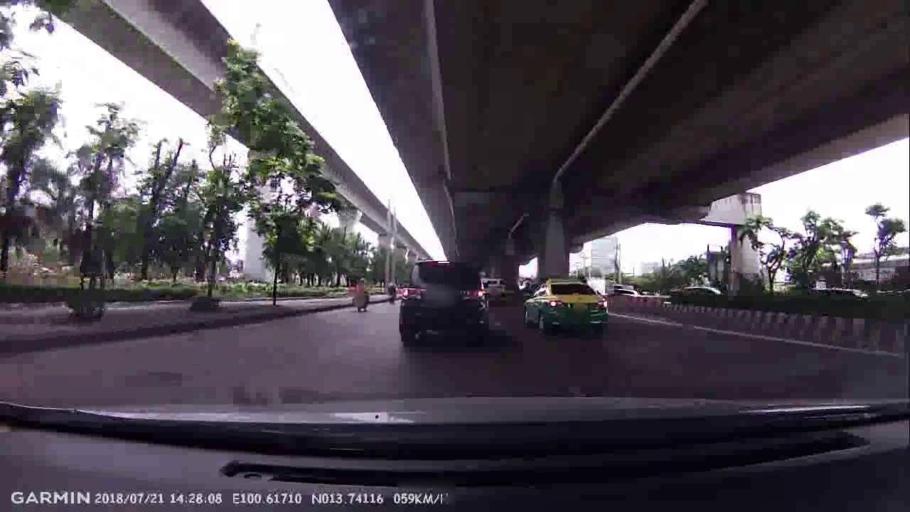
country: TH
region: Bangkok
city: Watthana
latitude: 13.7412
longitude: 100.6169
